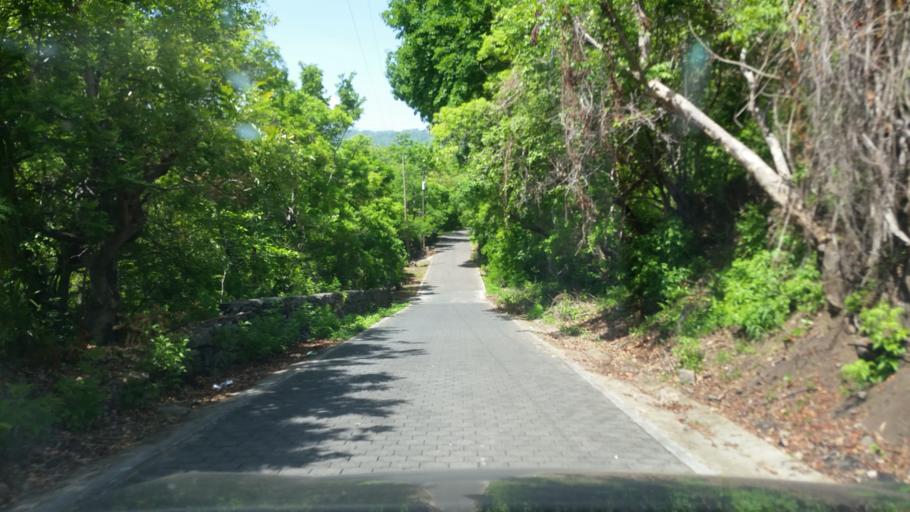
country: NI
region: Masaya
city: Catarina
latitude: 11.9279
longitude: -86.0553
